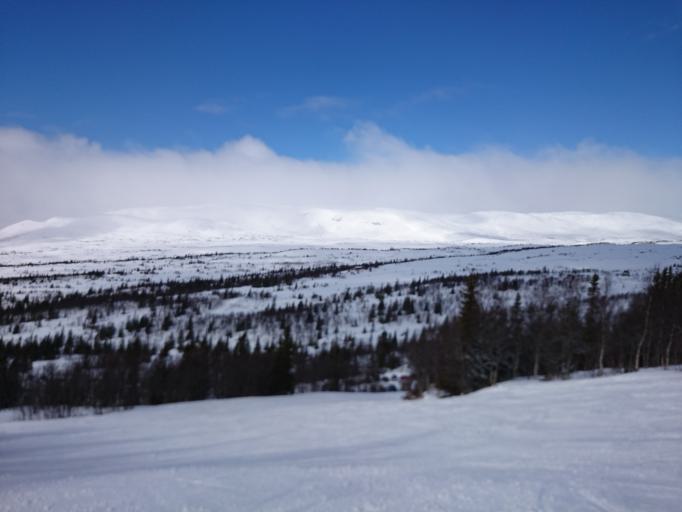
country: SE
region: Jaemtland
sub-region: Are Kommun
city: Are
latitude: 63.4296
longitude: 13.0197
